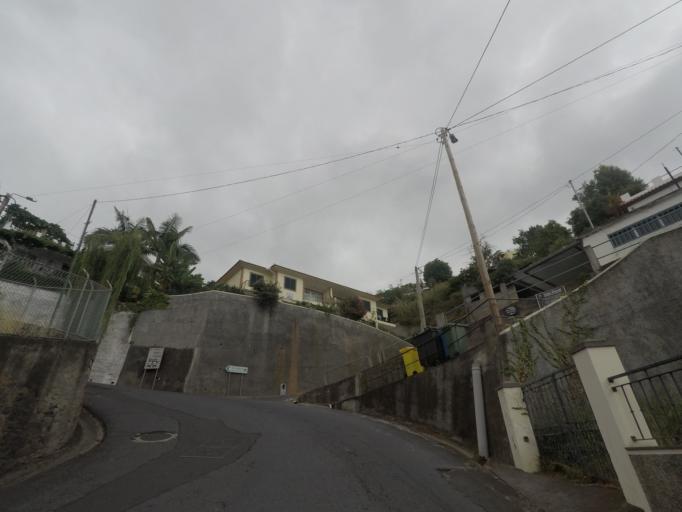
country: PT
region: Madeira
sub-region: Funchal
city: Nossa Senhora do Monte
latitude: 32.6639
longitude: -16.8934
